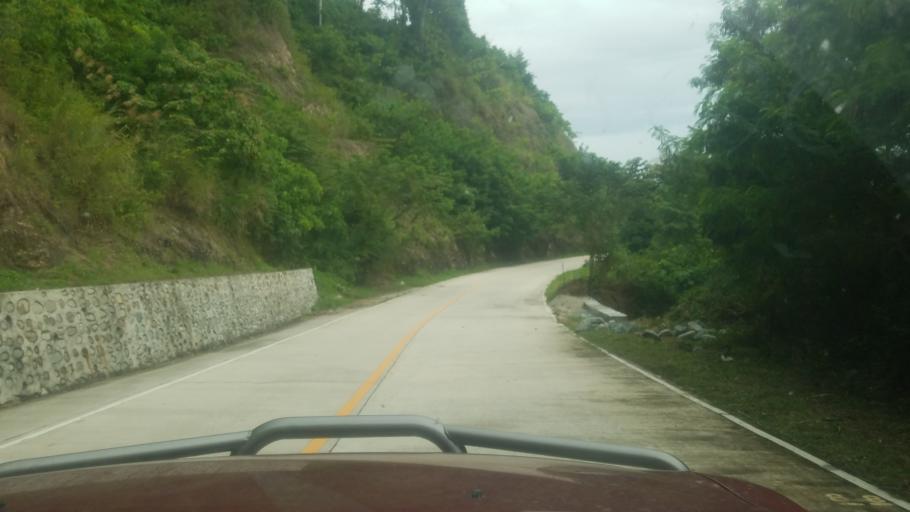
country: PH
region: Cagayan Valley
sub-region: Province of Quirino
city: Nagtipunan
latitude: 16.0436
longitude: 121.7149
